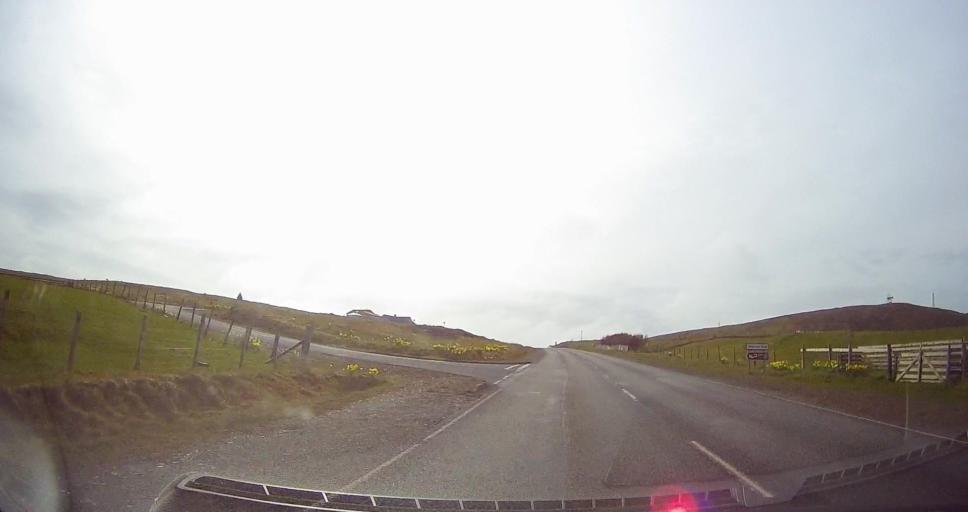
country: GB
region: Scotland
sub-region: Shetland Islands
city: Lerwick
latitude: 60.1385
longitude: -1.1960
